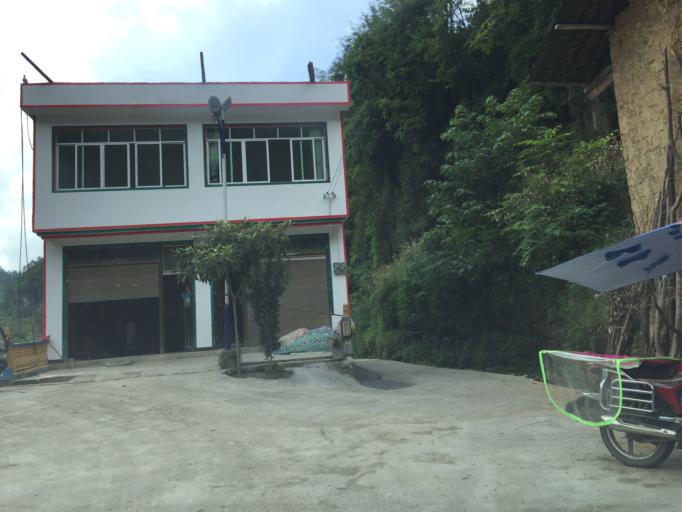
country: CN
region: Guizhou Sheng
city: Quankou
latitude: 28.5403
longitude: 108.1229
